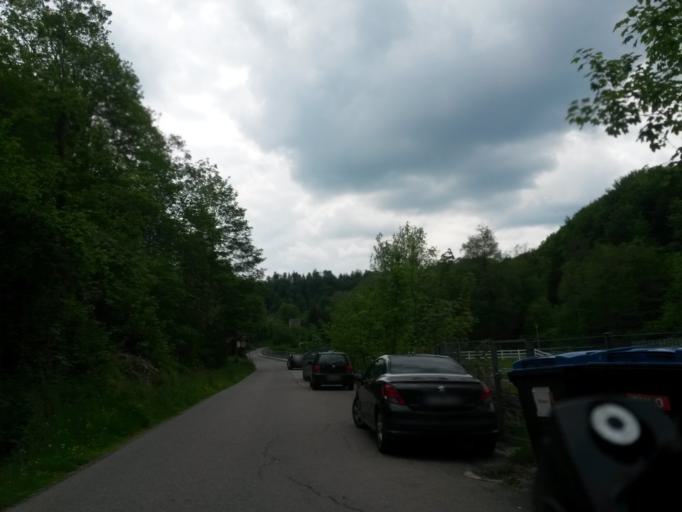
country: DE
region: Baden-Wuerttemberg
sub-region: Tuebingen Region
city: Wolfegg
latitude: 47.8386
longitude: 9.7865
